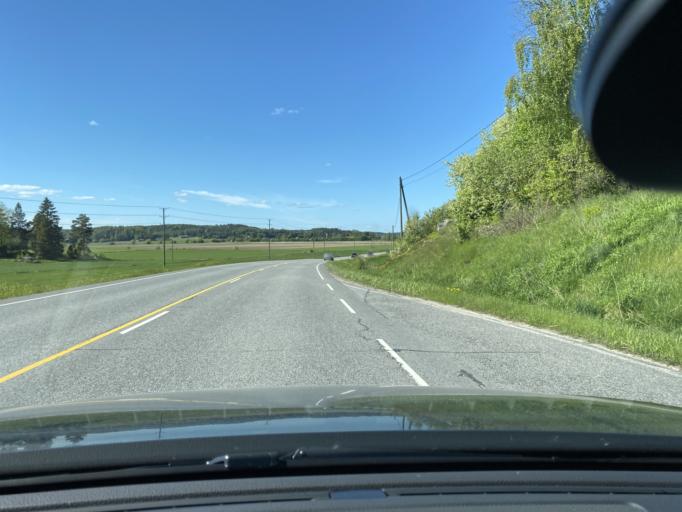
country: FI
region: Varsinais-Suomi
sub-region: Turku
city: Paimio
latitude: 60.4109
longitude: 22.6661
